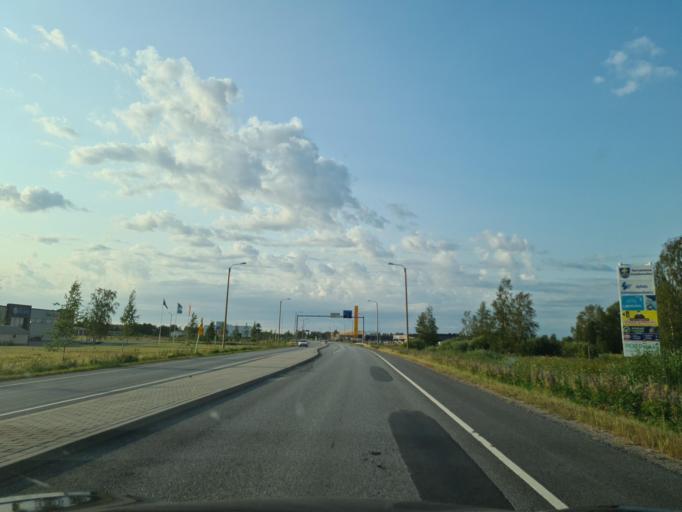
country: FI
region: Southern Ostrobothnia
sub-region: Seinaejoki
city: Kauhava
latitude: 63.0861
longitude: 23.0592
